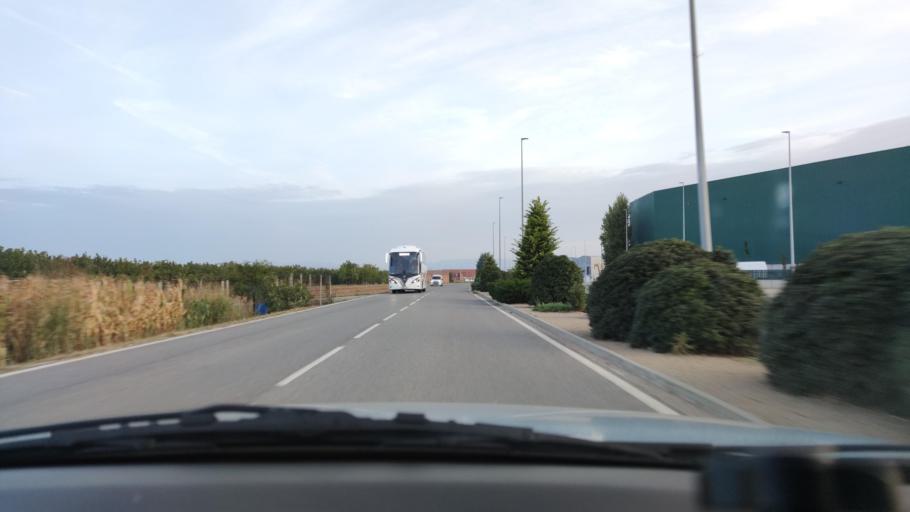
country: ES
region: Catalonia
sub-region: Provincia de Lleida
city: Mollerussa
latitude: 41.6435
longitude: 0.8764
